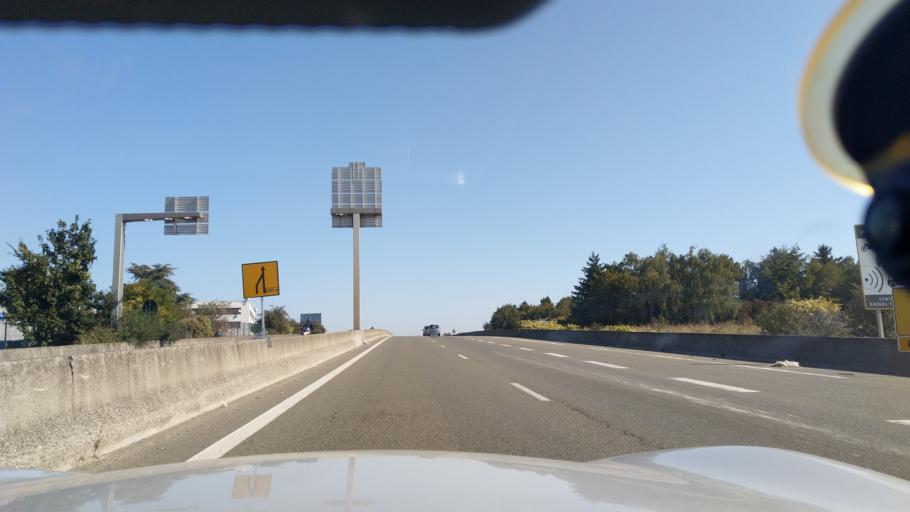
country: FR
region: Ile-de-France
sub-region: Departement du Val-d'Oise
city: Le Thillay
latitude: 48.9952
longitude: 2.4800
